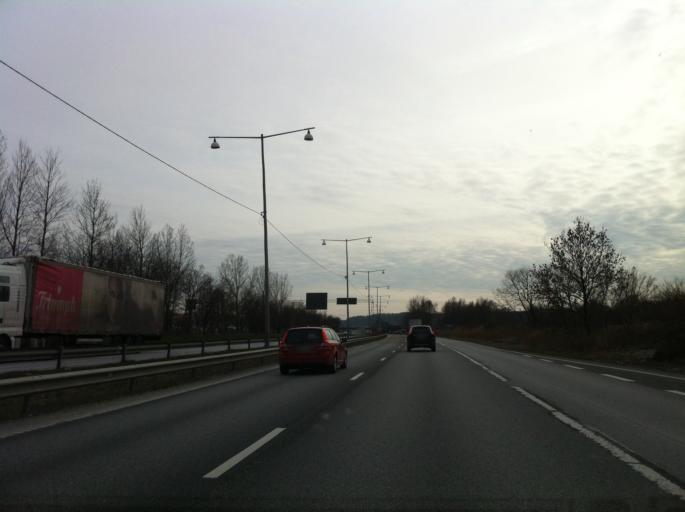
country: SE
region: Vaestra Goetaland
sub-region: Kungalvs Kommun
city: Kungalv
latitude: 57.8564
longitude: 11.9920
